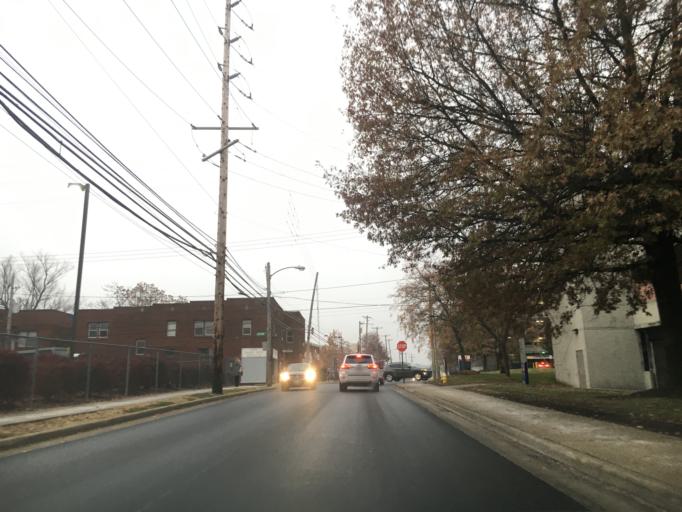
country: US
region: Ohio
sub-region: Summit County
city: Akron
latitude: 41.0805
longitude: -81.4983
